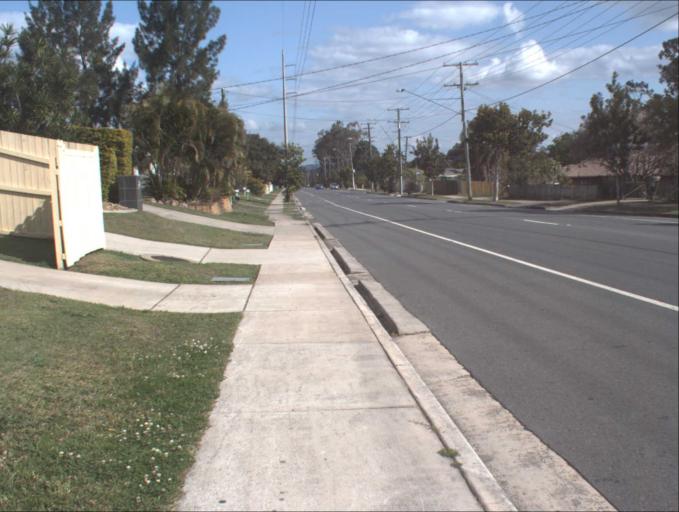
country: AU
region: Queensland
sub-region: Logan
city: Waterford West
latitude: -27.6874
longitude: 153.1204
